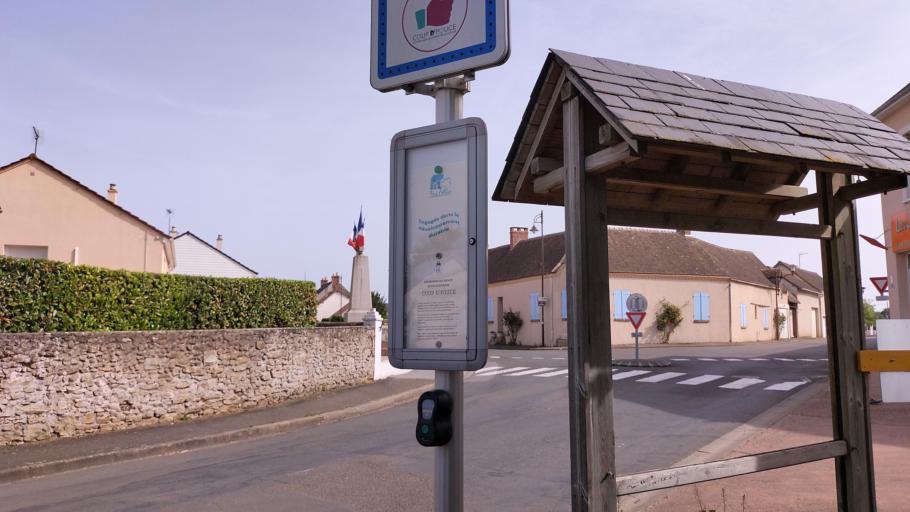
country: FR
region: Pays de la Loire
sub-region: Departement de la Sarthe
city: Souligne-sous-Ballon
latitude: 48.1099
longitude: 0.2170
